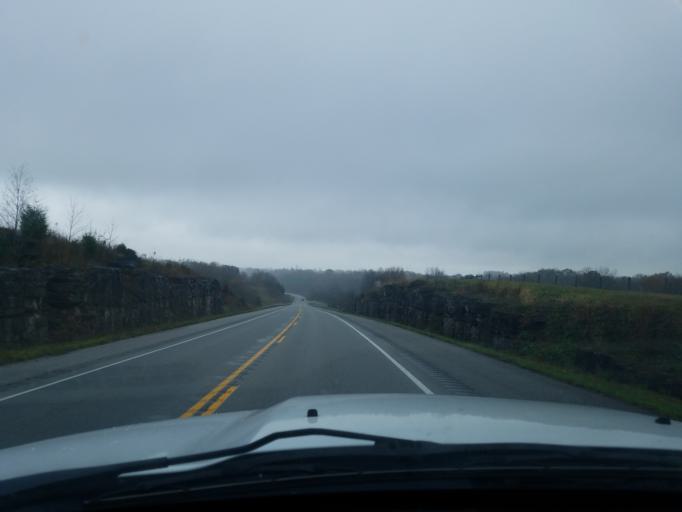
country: US
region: Kentucky
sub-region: Taylor County
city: Campbellsville
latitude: 37.3926
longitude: -85.4568
